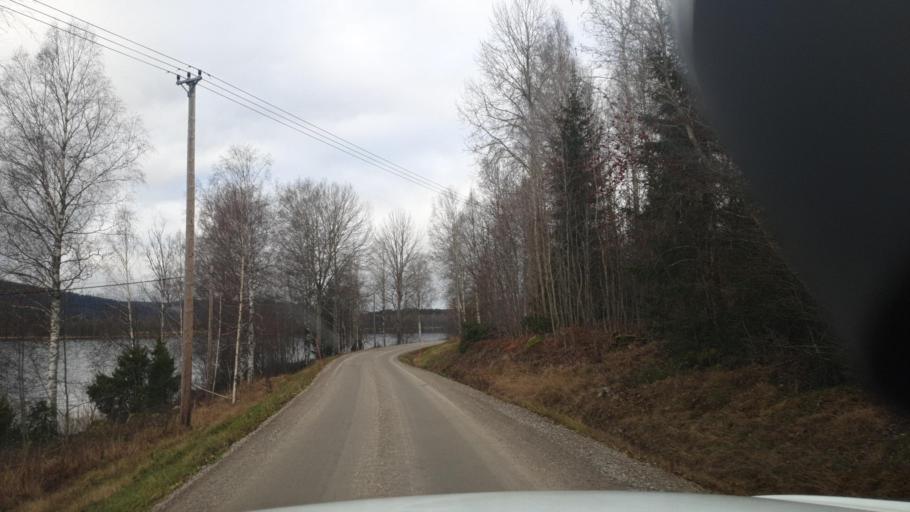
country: SE
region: Vaermland
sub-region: Arvika Kommun
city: Arvika
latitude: 59.7348
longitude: 12.8315
